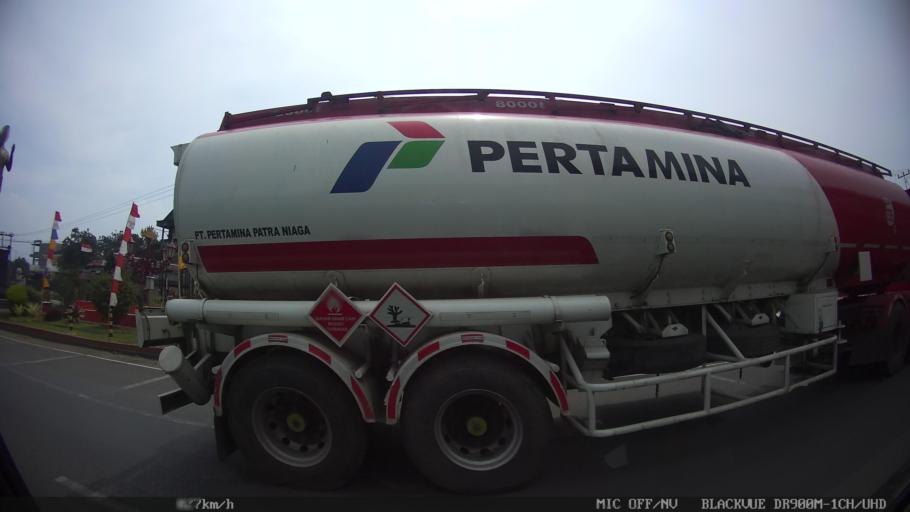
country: ID
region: Lampung
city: Bandarlampung
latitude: -5.4321
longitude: 105.2752
